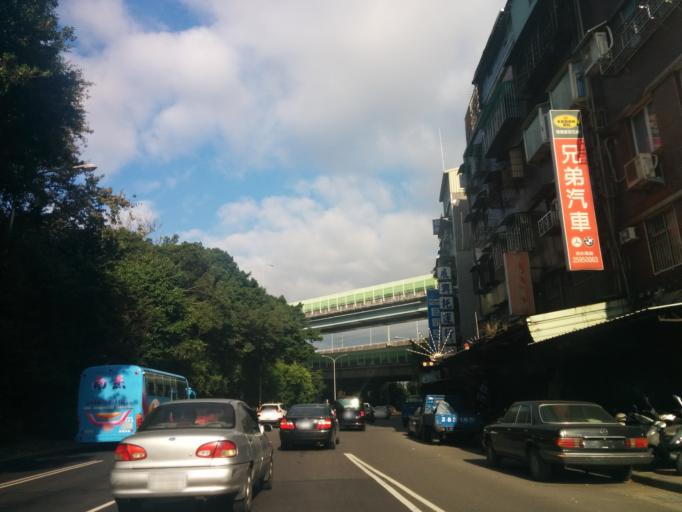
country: TW
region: Taipei
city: Taipei
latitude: 25.0772
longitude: 121.5094
